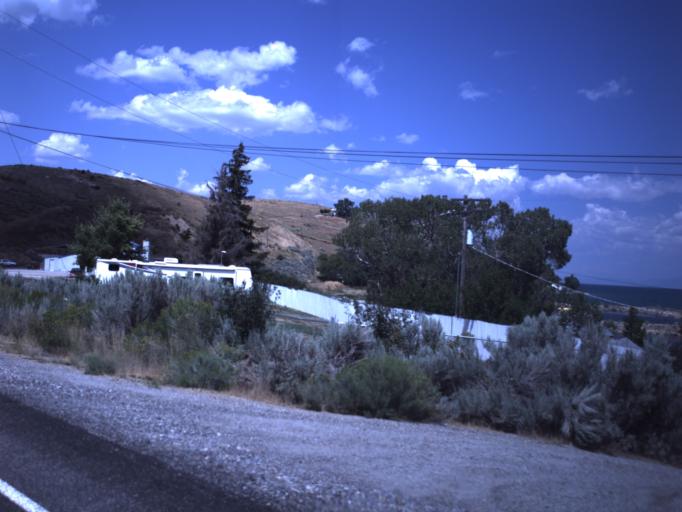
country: US
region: Utah
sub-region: Rich County
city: Randolph
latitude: 41.8992
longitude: -111.3696
